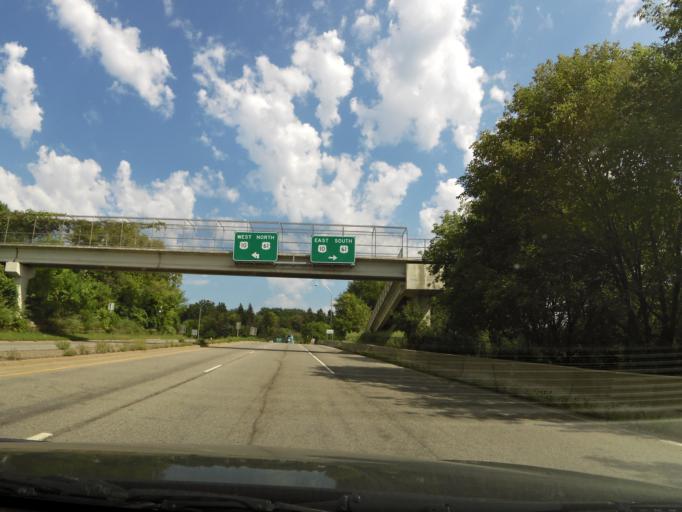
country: US
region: Minnesota
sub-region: Ramsey County
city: Maplewood
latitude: 44.9465
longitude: -93.0431
